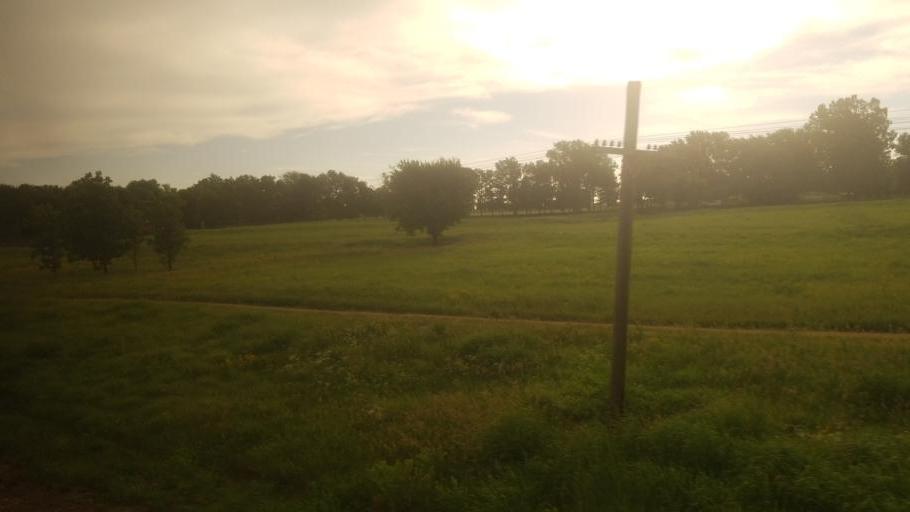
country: US
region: Kansas
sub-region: Osage County
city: Carbondale
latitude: 38.8609
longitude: -95.6992
